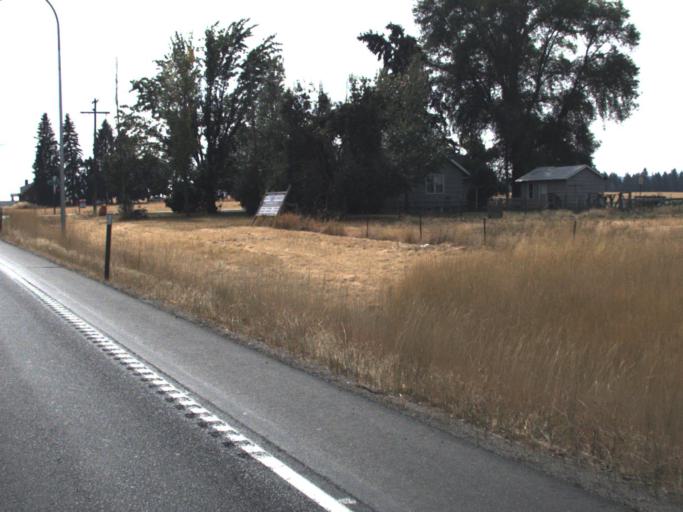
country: US
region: Washington
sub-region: Spokane County
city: Deer Park
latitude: 47.8755
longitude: -117.4223
